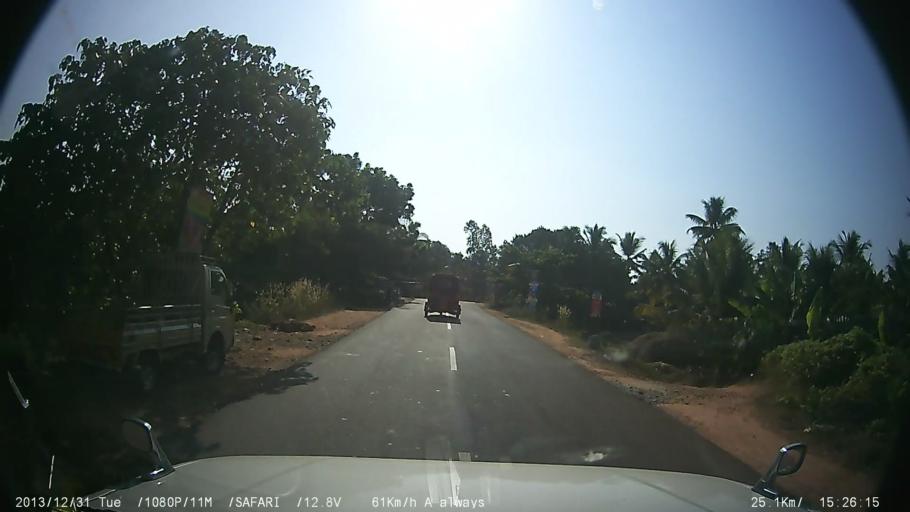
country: IN
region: Kerala
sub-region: Kottayam
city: Vaikam
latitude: 9.6844
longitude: 76.4619
